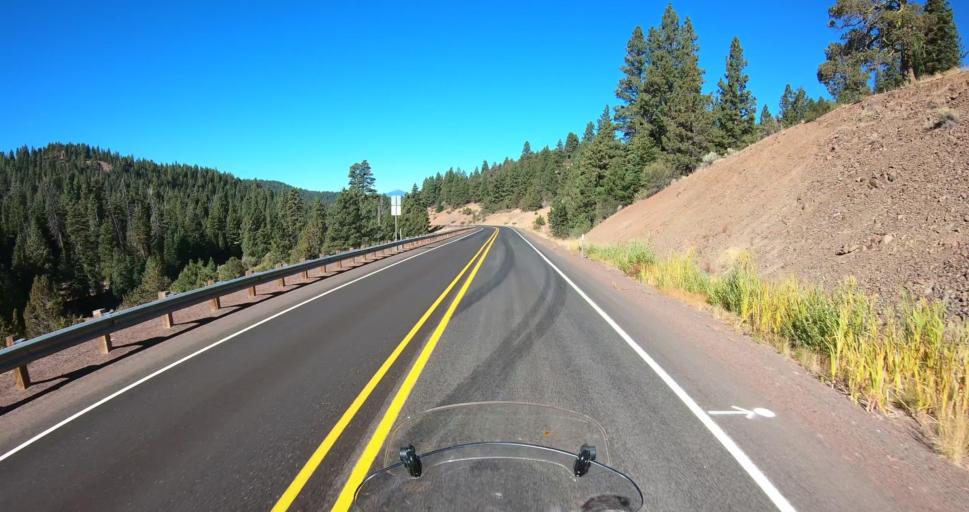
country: US
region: Oregon
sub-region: Lake County
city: Lakeview
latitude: 42.2387
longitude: -120.3017
